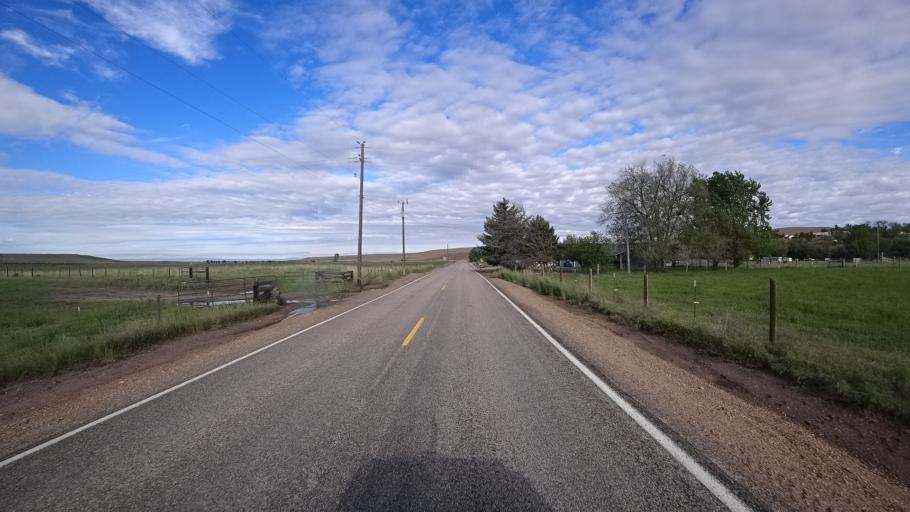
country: US
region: Idaho
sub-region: Ada County
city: Star
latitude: 43.7718
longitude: -116.4876
